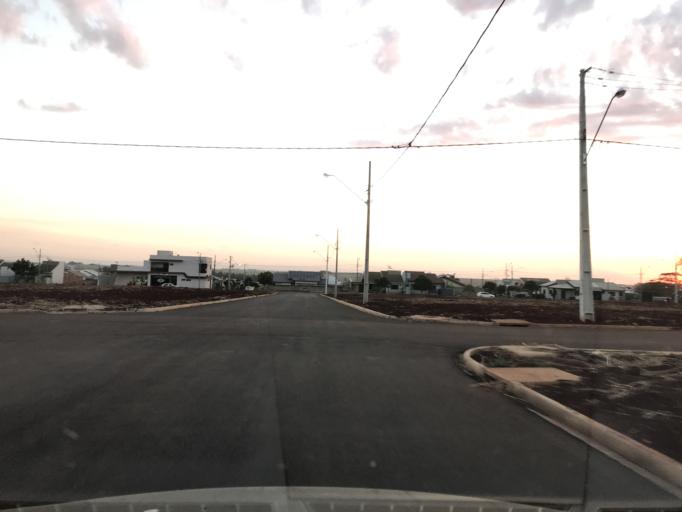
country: BR
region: Parana
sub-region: Palotina
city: Palotina
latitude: -24.3024
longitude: -53.8362
